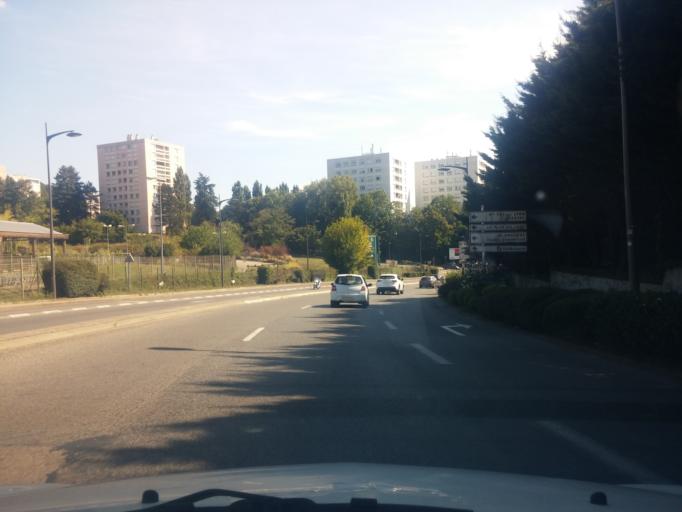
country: FR
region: Rhone-Alpes
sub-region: Departement du Rhone
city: Francheville
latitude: 45.7360
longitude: 4.7761
